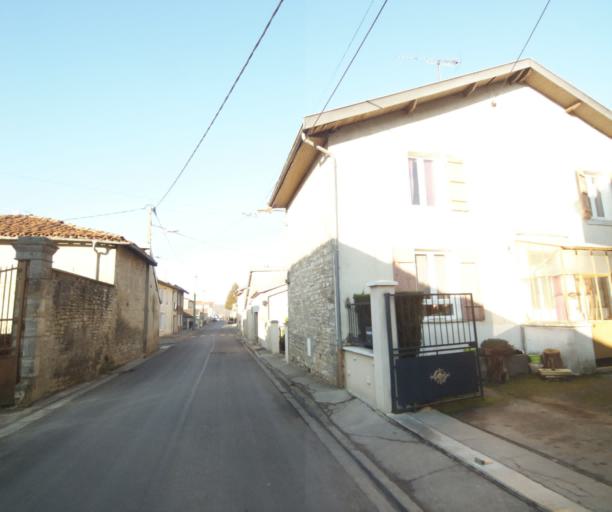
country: FR
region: Champagne-Ardenne
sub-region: Departement de la Haute-Marne
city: Bienville
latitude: 48.5746
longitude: 5.0455
